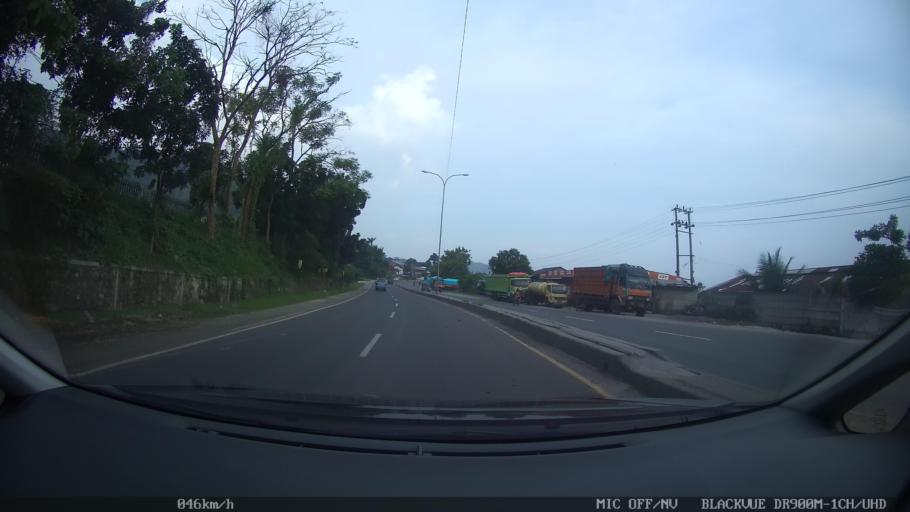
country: ID
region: Lampung
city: Bandarlampung
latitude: -5.4343
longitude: 105.2977
